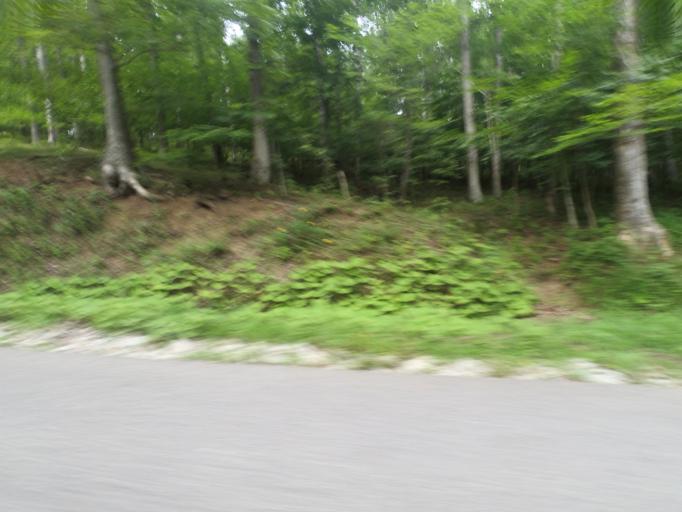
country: US
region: West Virginia
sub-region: Cabell County
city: Huntington
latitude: 38.3821
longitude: -82.4128
